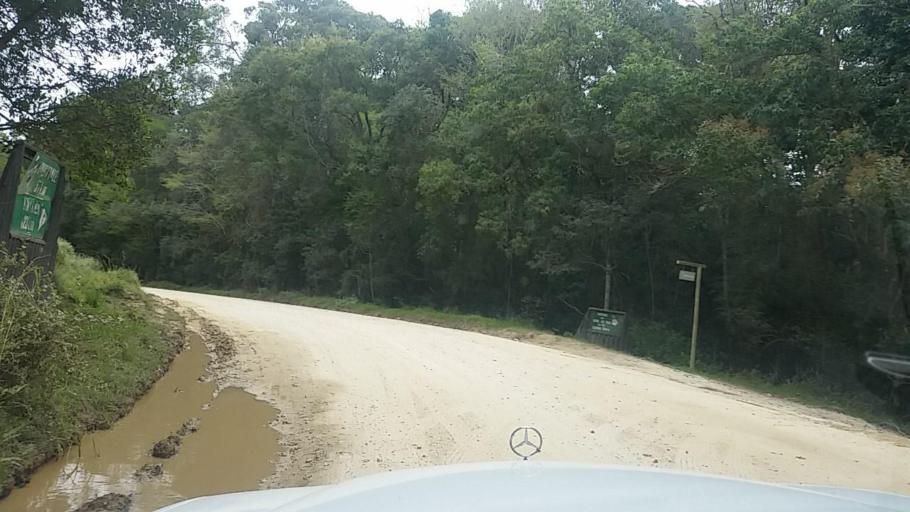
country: ZA
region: Western Cape
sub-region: Eden District Municipality
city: Knysna
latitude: -33.9496
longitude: 23.1488
